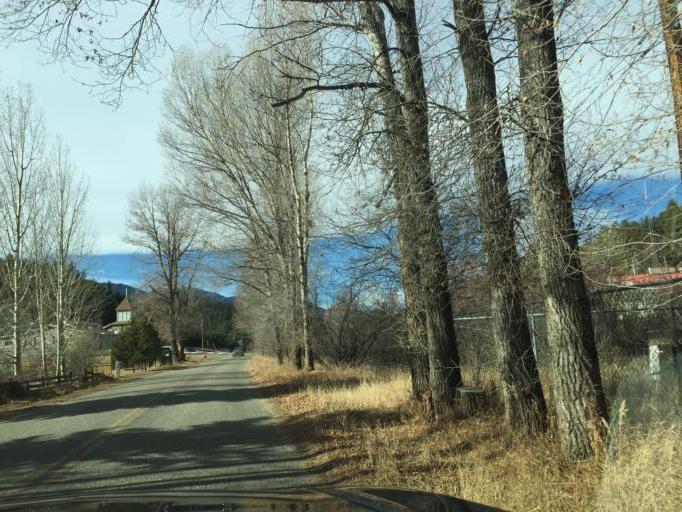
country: US
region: Colorado
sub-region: Jefferson County
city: Evergreen
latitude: 39.4060
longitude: -105.4811
